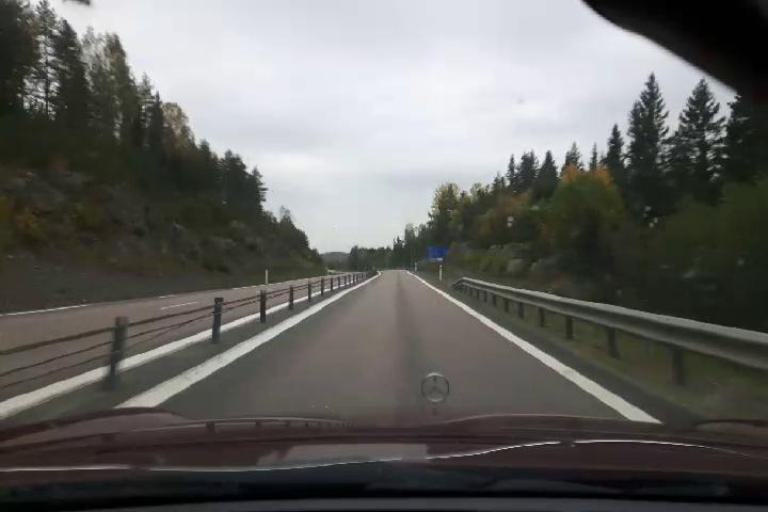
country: SE
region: Vaesternorrland
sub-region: Kramfors Kommun
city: Nordingra
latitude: 62.9356
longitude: 18.0937
